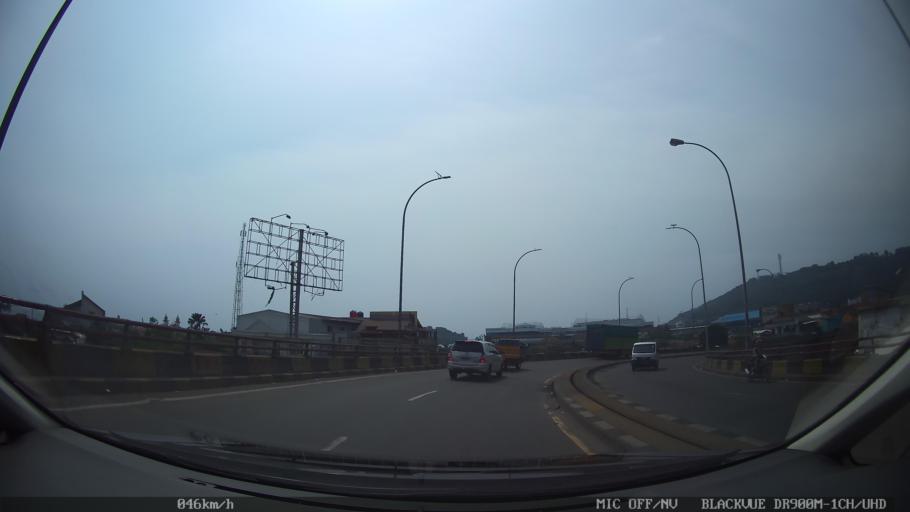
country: ID
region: Banten
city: Curug
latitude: -5.9396
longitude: 106.0020
